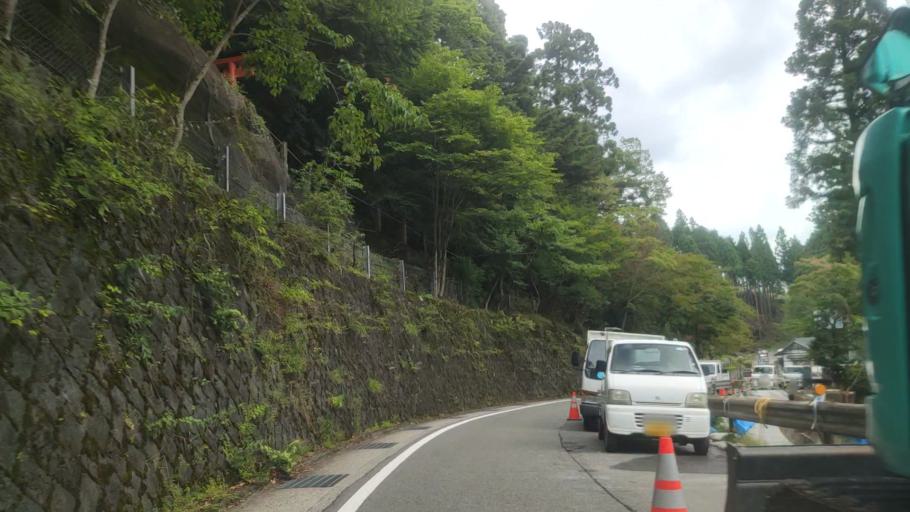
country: JP
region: Wakayama
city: Koya
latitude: 34.2138
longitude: 135.5722
